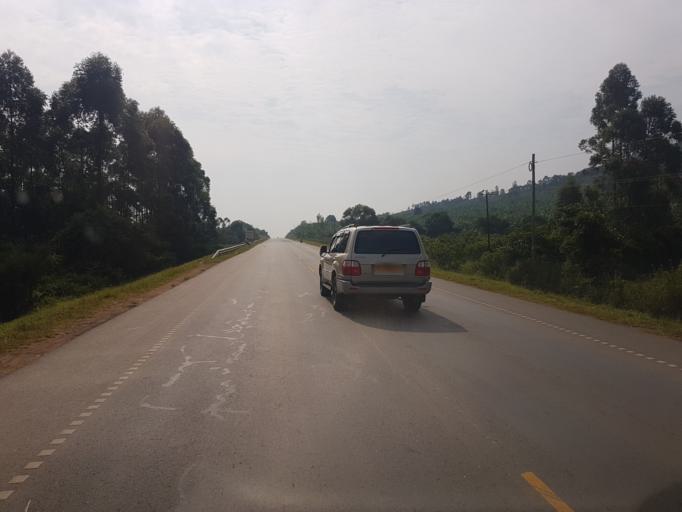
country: UG
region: Western Region
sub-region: Sheema District
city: Kibingo
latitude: -0.6393
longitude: 30.5100
